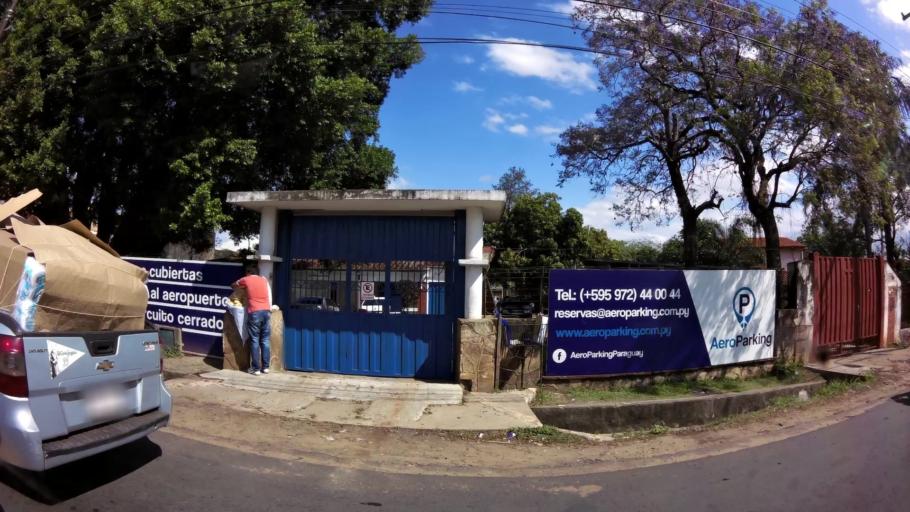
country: PY
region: Central
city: Fernando de la Mora
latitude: -25.2638
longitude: -57.5164
